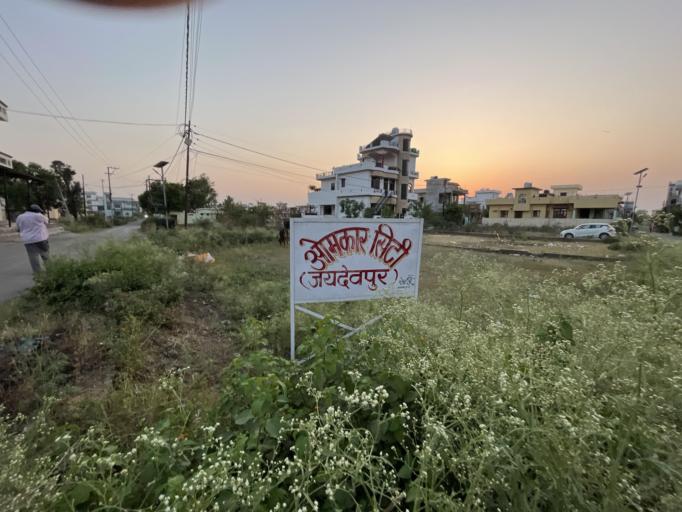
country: IN
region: Uttarakhand
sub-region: Naini Tal
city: Haldwani
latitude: 29.2108
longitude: 79.4866
